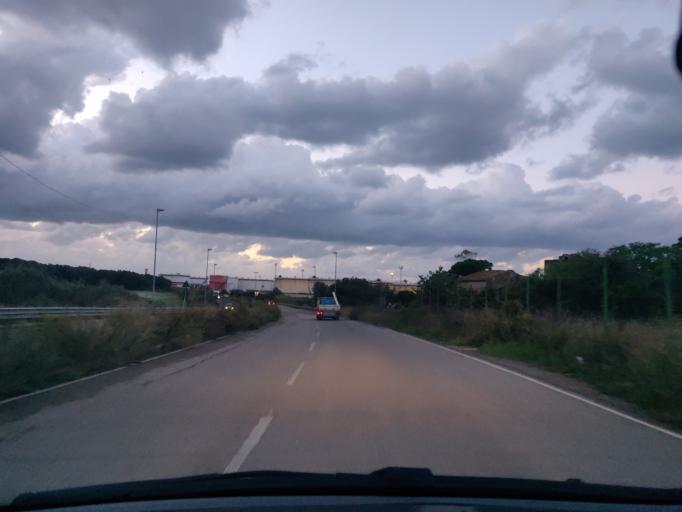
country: IT
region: Latium
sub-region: Citta metropolitana di Roma Capitale
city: Aurelia
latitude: 42.1156
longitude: 11.7789
